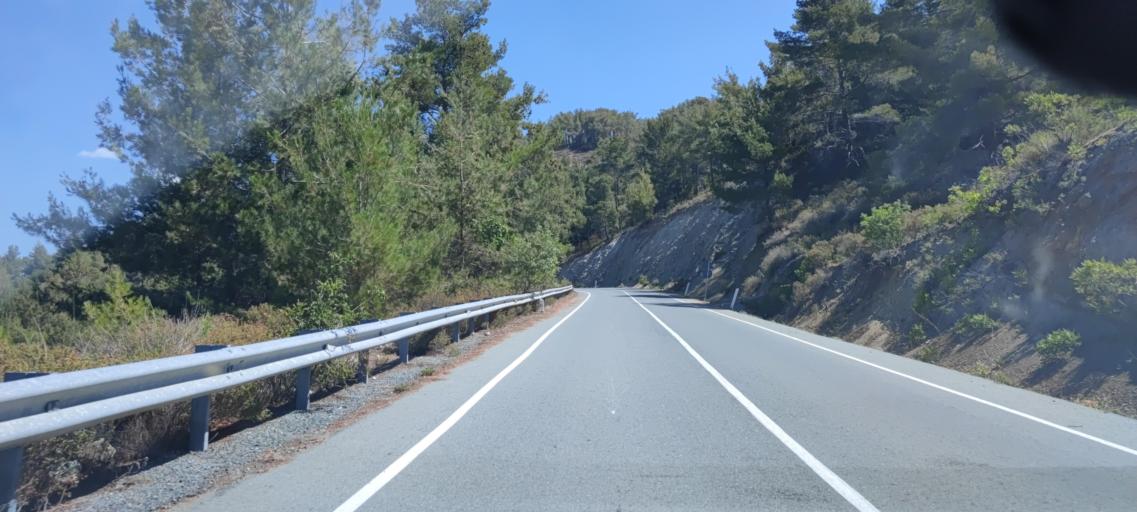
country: CY
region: Lefkosia
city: Kakopetria
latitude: 34.9132
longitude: 32.8148
